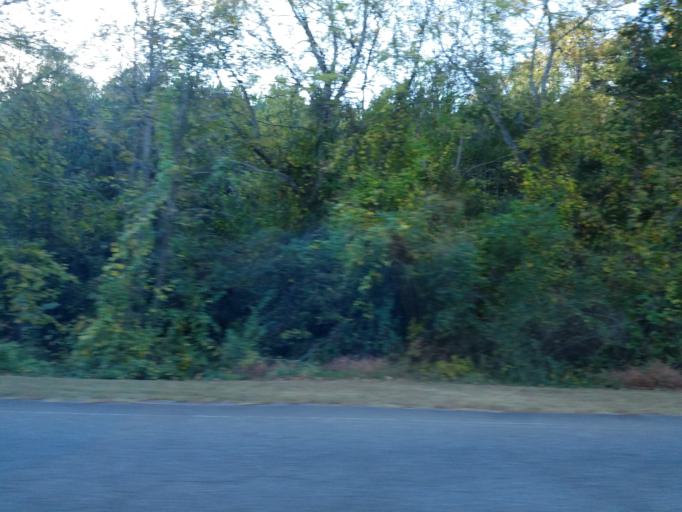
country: US
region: Georgia
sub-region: Bartow County
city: Adairsville
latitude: 34.3152
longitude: -84.9371
